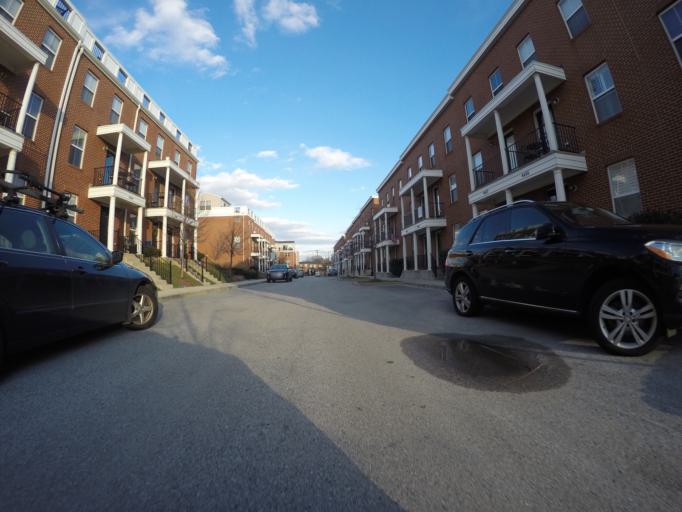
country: US
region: Maryland
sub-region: Baltimore County
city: Dundalk
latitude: 39.2819
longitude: -76.5573
